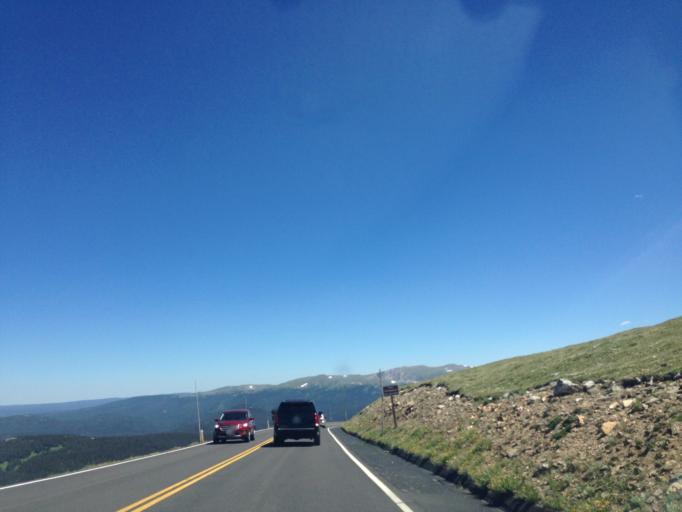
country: US
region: Colorado
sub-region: Larimer County
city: Estes Park
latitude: 40.4335
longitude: -105.7683
